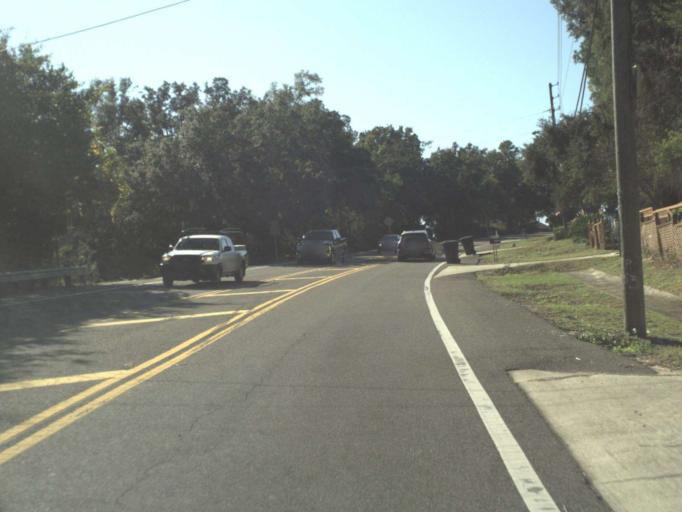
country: US
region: Florida
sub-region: Escambia County
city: Ferry Pass
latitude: 30.4901
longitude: -87.1557
